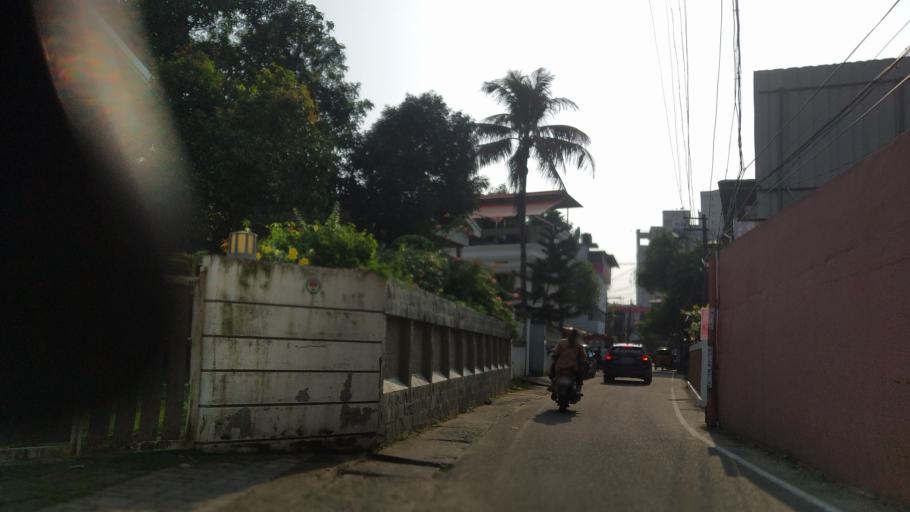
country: IN
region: Kerala
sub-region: Ernakulam
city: Cochin
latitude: 9.9981
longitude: 76.2927
